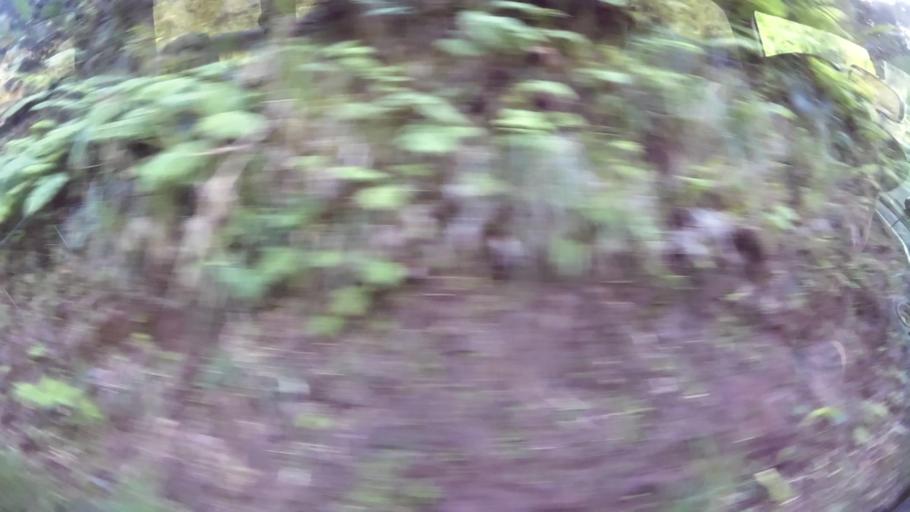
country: DM
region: Saint Paul
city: Pont Casse
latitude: 15.3447
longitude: -61.3698
